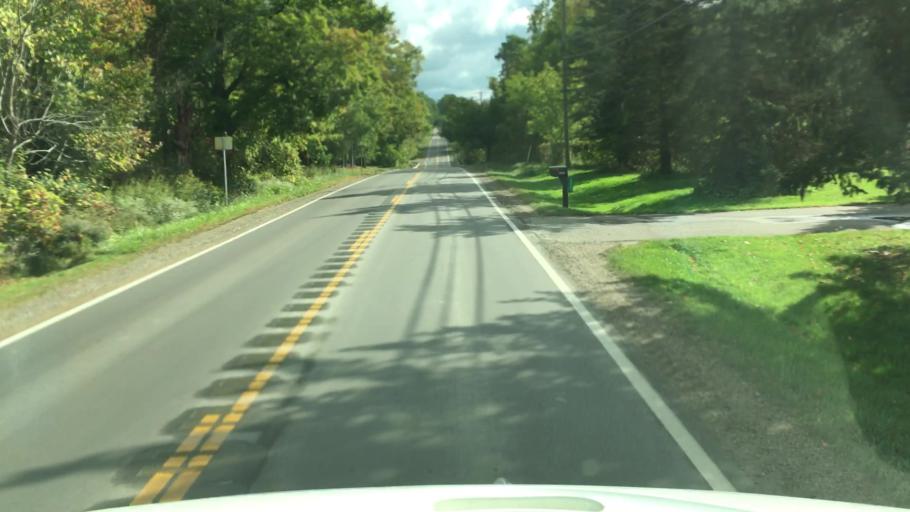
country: US
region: Michigan
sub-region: Oakland County
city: Oxford
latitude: 42.8675
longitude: -83.3338
